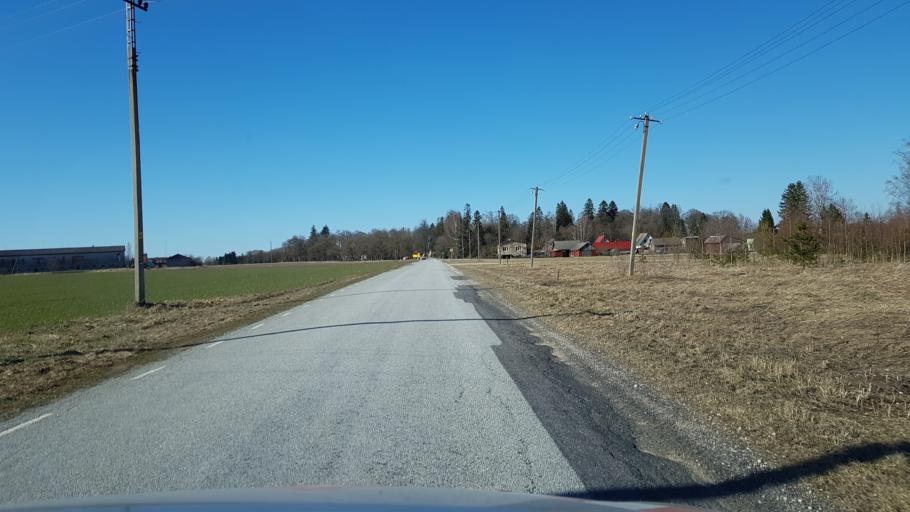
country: EE
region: Laeaene-Virumaa
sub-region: Viru-Nigula vald
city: Kunda
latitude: 59.3886
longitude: 26.5710
